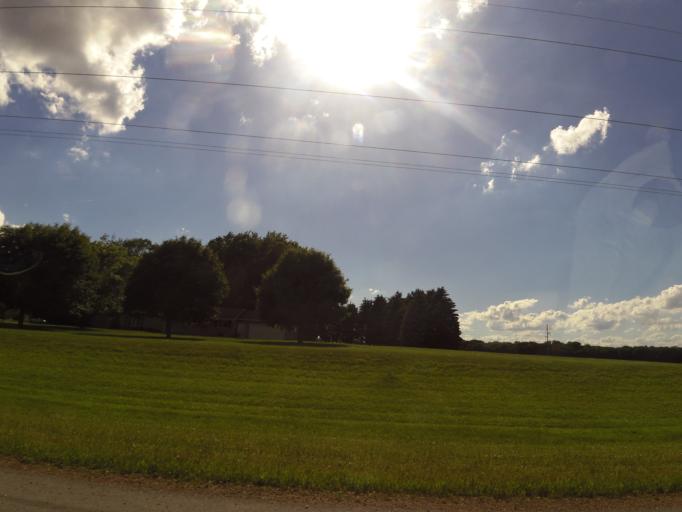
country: US
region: Minnesota
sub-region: Carver County
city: Waconia
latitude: 44.8940
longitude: -93.8185
